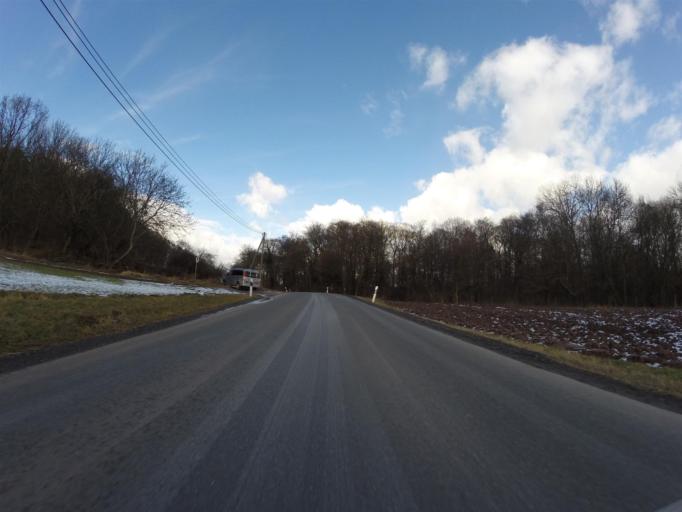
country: DE
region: Thuringia
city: Grosslobichau
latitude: 50.9357
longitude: 11.6888
